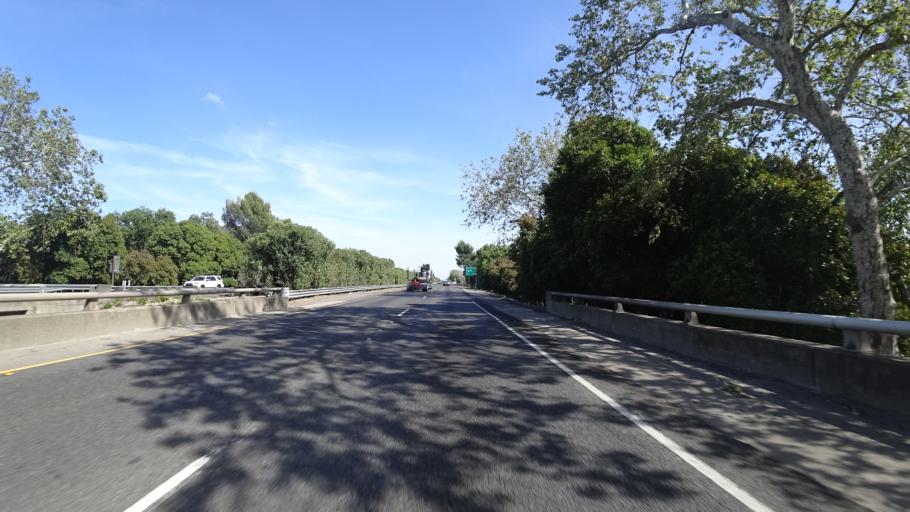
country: US
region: California
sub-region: Butte County
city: Chico
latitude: 39.7481
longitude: -121.8355
